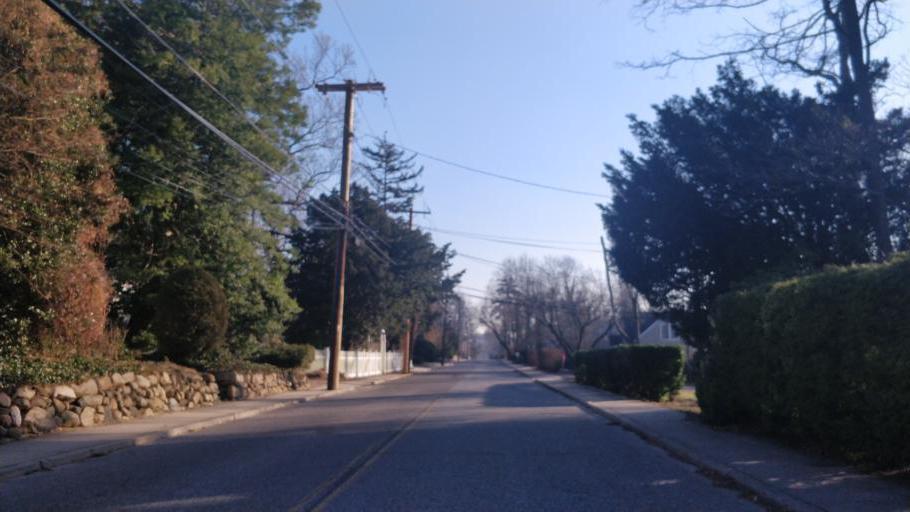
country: US
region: New York
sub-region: Nassau County
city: Bayville
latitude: 40.9045
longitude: -73.5710
